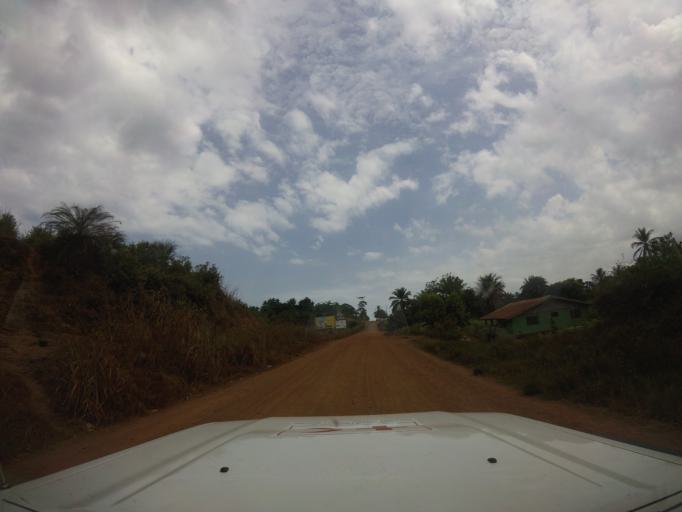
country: LR
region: Grand Cape Mount
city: Robertsport
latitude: 6.7508
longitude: -11.3619
